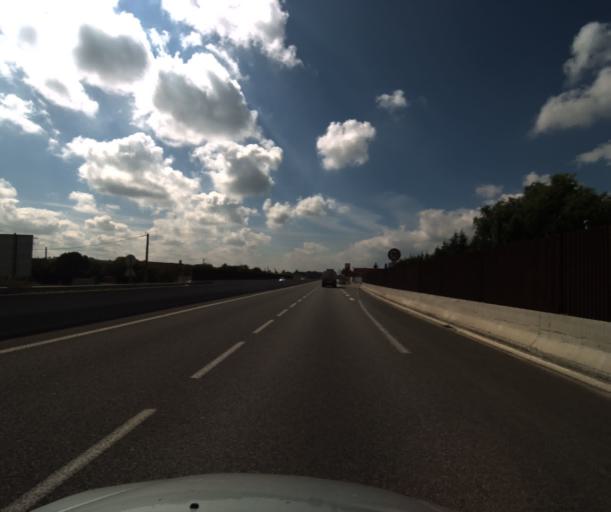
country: FR
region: Midi-Pyrenees
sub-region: Departement de la Haute-Garonne
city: Labarthe-sur-Leze
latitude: 43.4561
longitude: 1.4163
